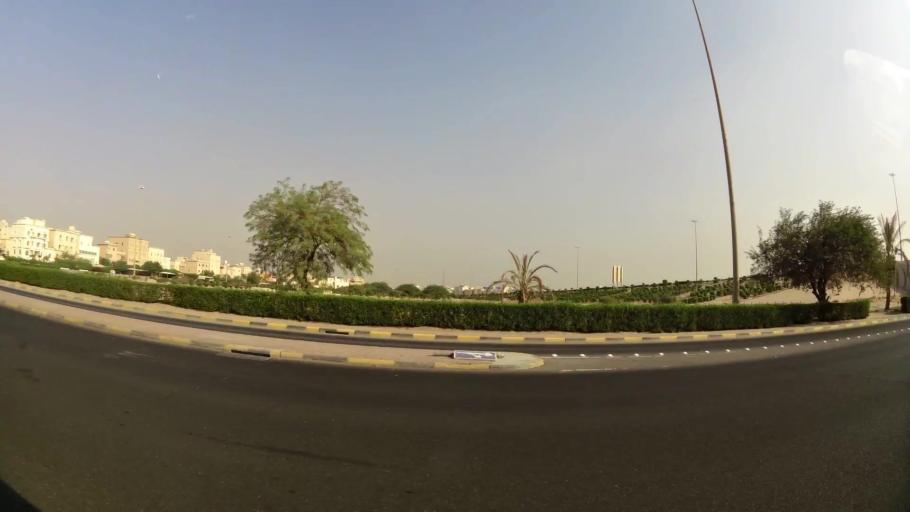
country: KW
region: Mubarak al Kabir
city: Mubarak al Kabir
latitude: 29.1805
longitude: 48.0895
